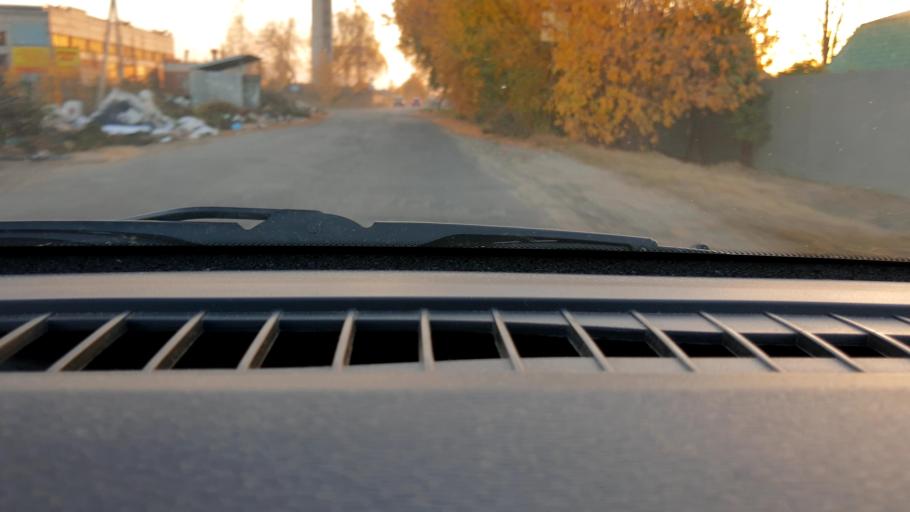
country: RU
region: Nizjnij Novgorod
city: Kstovo
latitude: 56.1865
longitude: 44.1548
